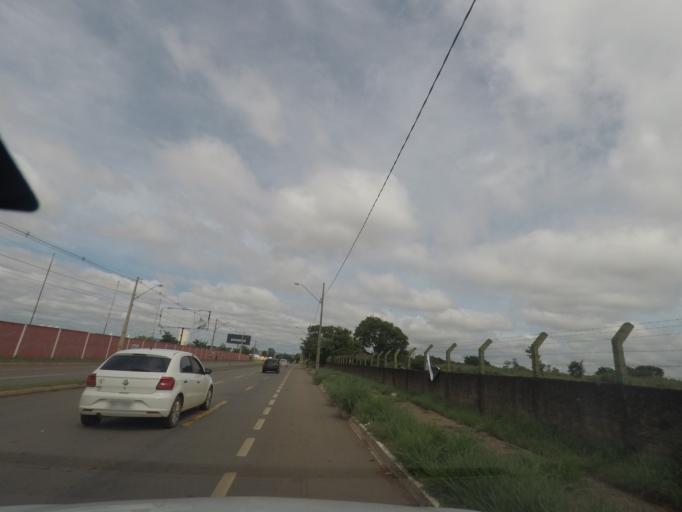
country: BR
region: Goias
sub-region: Goiania
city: Goiania
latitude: -16.6437
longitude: -49.2140
